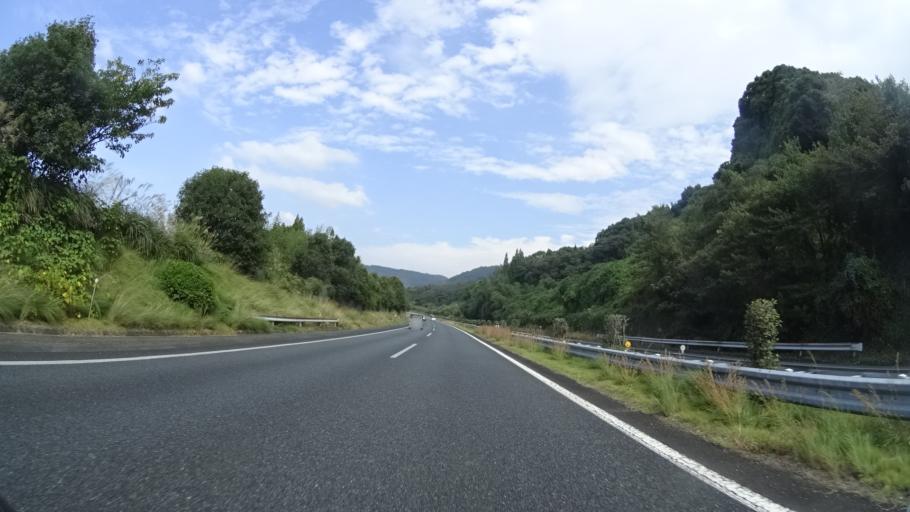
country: JP
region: Kumamoto
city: Matsubase
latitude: 32.5982
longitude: 130.7192
